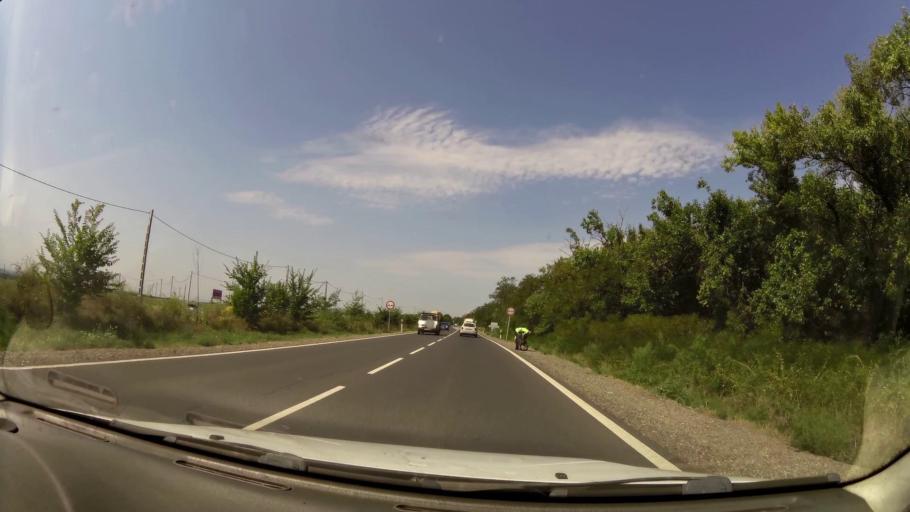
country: HU
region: Pest
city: Maglod
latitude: 47.4536
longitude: 19.3545
